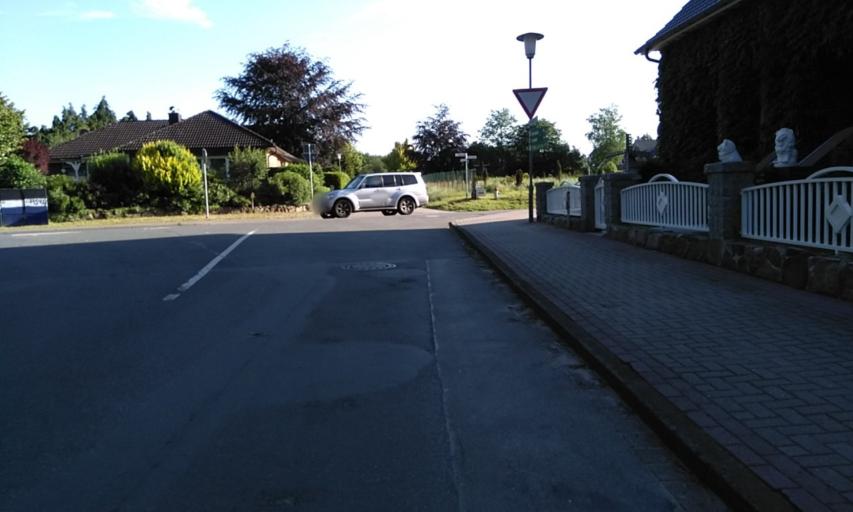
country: DE
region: Lower Saxony
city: Deinste
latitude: 53.5306
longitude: 9.4433
